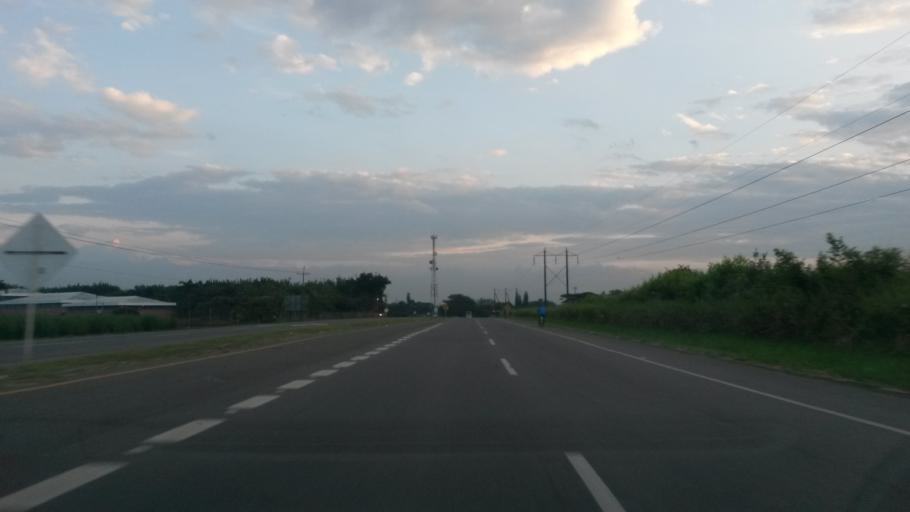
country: CO
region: Cauca
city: Santander de Quilichao
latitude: 3.0740
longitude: -76.4752
